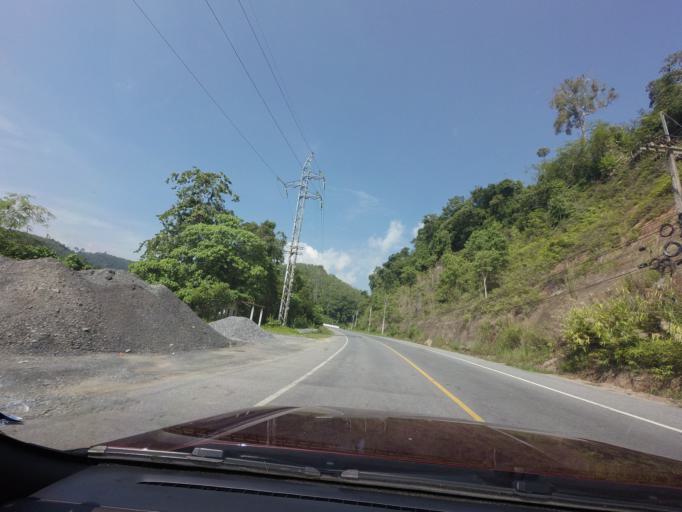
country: TH
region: Yala
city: Than To
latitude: 5.9587
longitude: 101.1932
